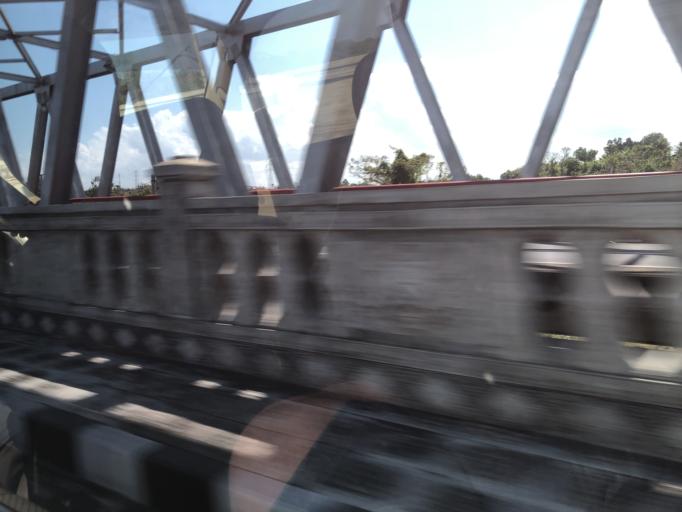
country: ID
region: Bali
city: Dawan
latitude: -8.5598
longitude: 115.4243
